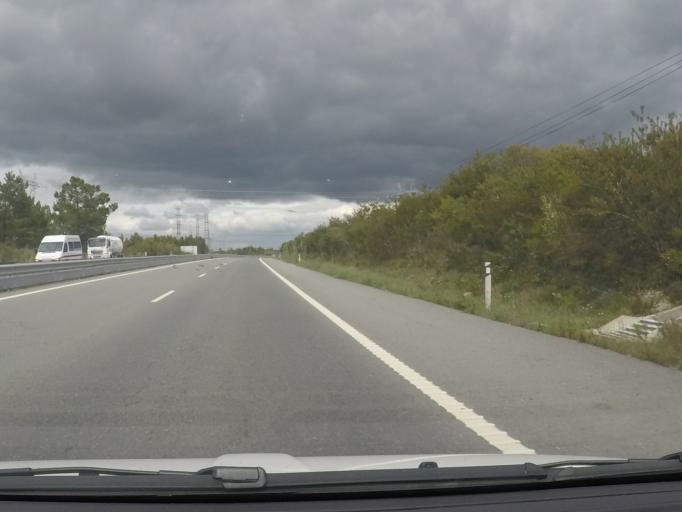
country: PT
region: Setubal
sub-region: Santiago do Cacem
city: Santo Andre
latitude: 37.9920
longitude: -8.7672
